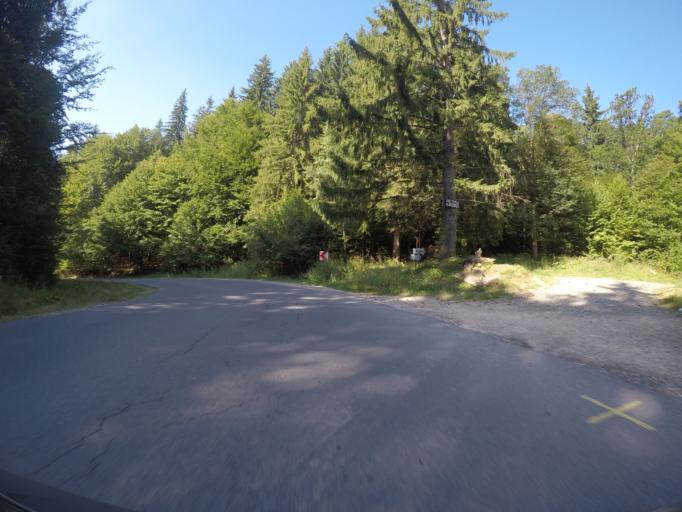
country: RO
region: Brasov
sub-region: Comuna Cristian
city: Cristian
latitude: 45.5995
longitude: 25.5425
